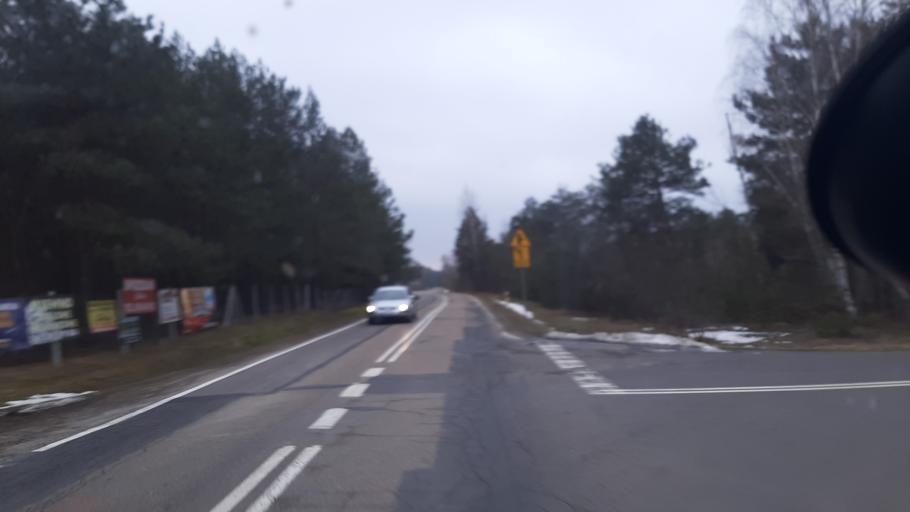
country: PL
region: Lublin Voivodeship
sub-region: Powiat wlodawski
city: Wlodawa
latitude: 51.5176
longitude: 23.5700
